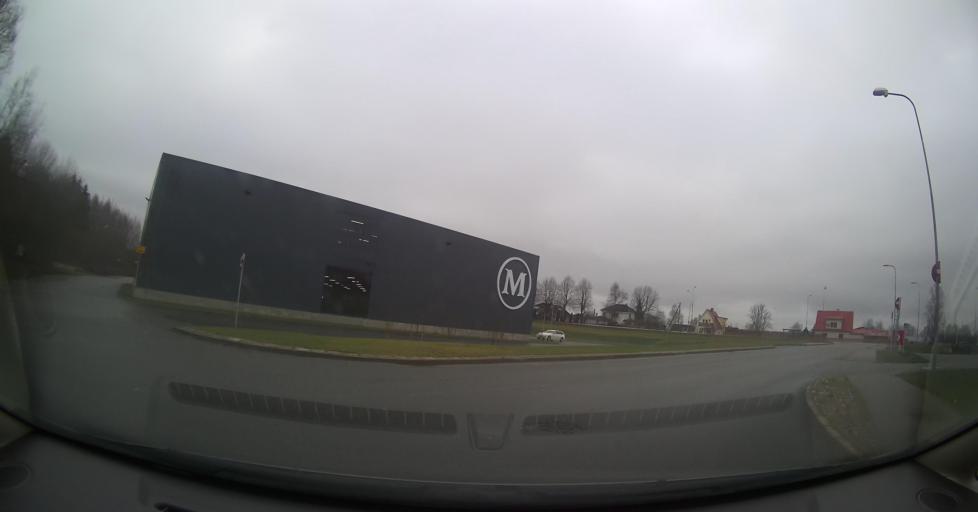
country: EE
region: Tartu
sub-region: Tartu linn
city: Tartu
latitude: 58.4065
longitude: 26.7111
